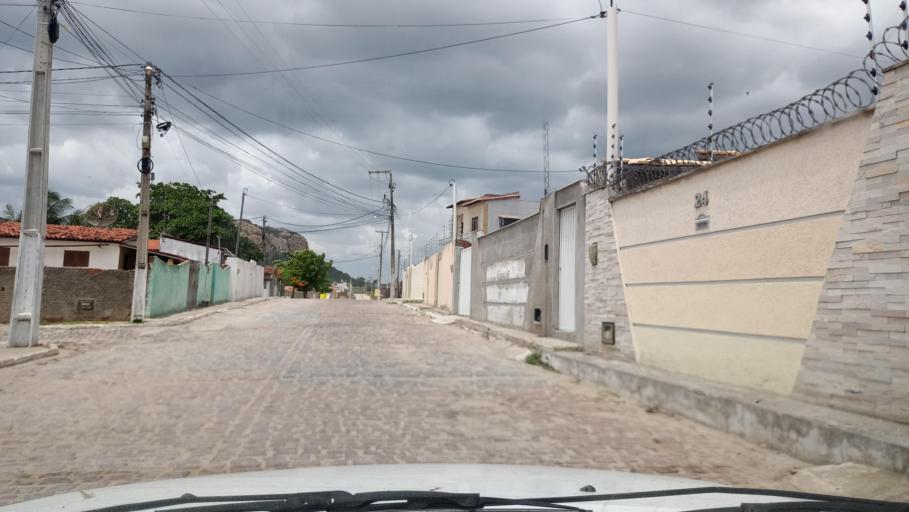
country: BR
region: Rio Grande do Norte
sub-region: Tangara
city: Tangara
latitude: -6.0991
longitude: -35.7113
